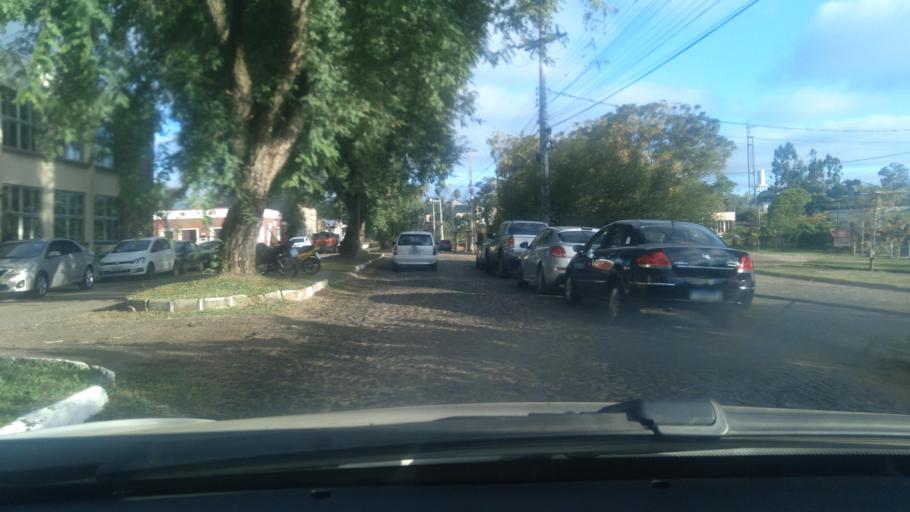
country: BR
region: Rio Grande do Sul
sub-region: Rosario Do Sul
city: Rosario do Sul
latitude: -30.2613
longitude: -54.9203
